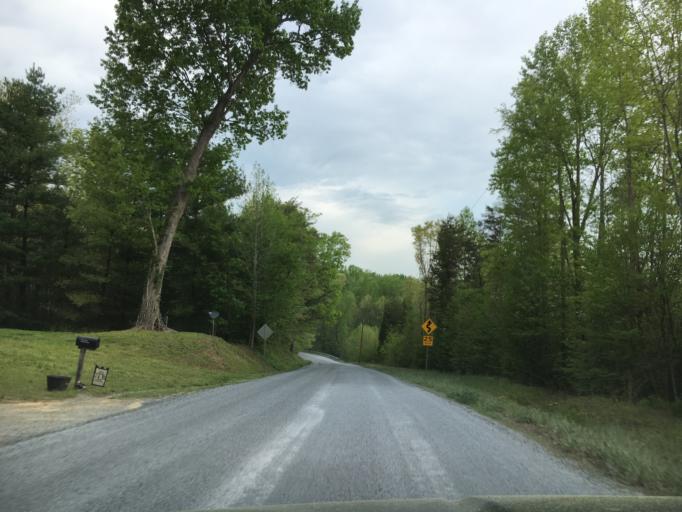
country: US
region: Virginia
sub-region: Campbell County
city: Brookneal
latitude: 36.9438
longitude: -78.9517
